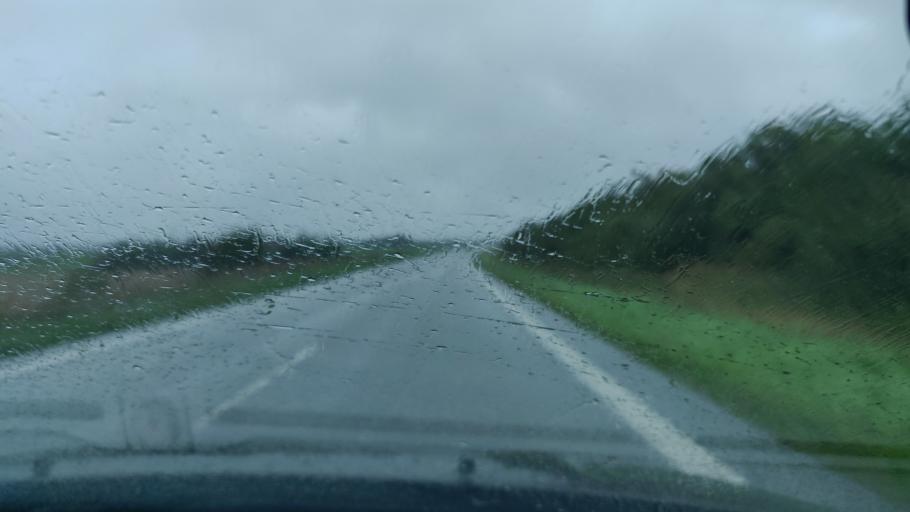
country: DK
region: North Denmark
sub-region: Thisted Kommune
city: Hurup
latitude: 56.8218
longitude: 8.4943
